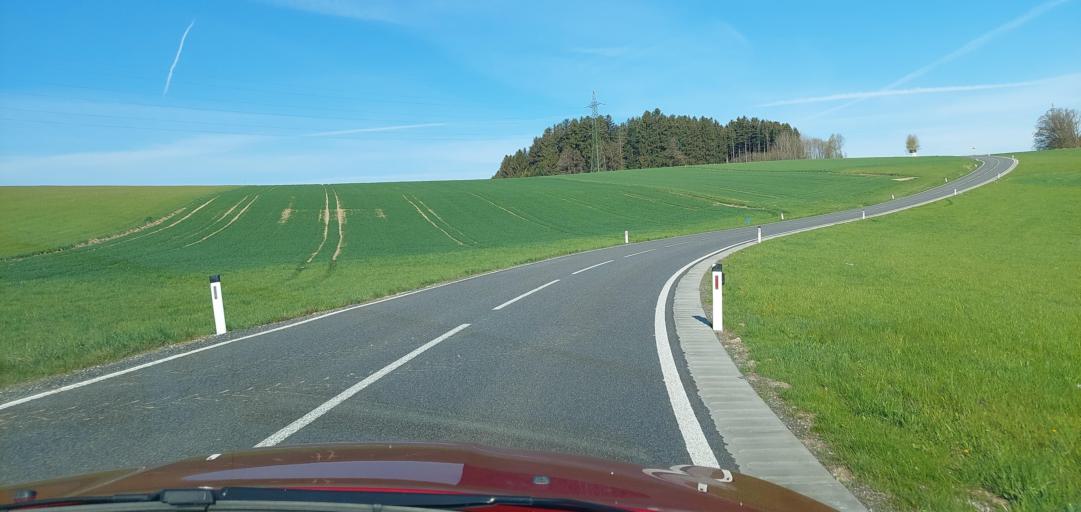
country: AT
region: Upper Austria
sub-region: Politischer Bezirk Ried im Innkreis
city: Ried im Innkreis
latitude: 48.1766
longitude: 13.5355
